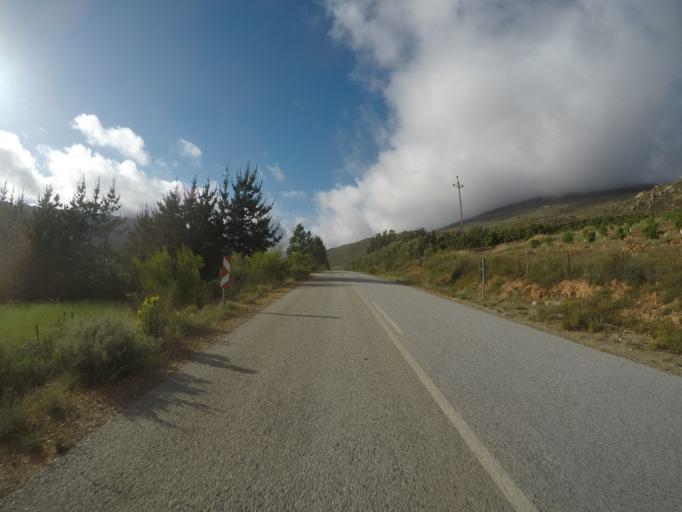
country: ZA
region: Western Cape
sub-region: West Coast District Municipality
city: Clanwilliam
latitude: -32.3581
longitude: 18.8528
